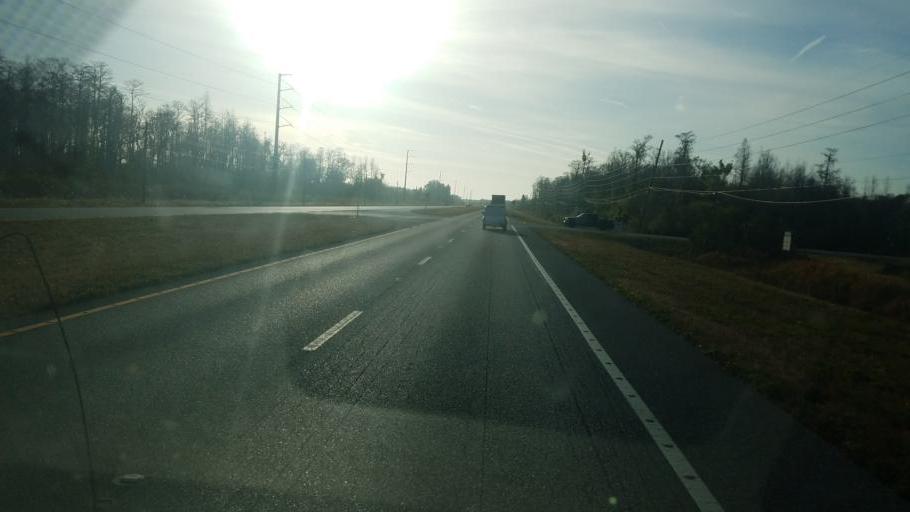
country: US
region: Florida
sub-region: Osceola County
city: Saint Cloud
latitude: 28.1602
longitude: -81.1157
